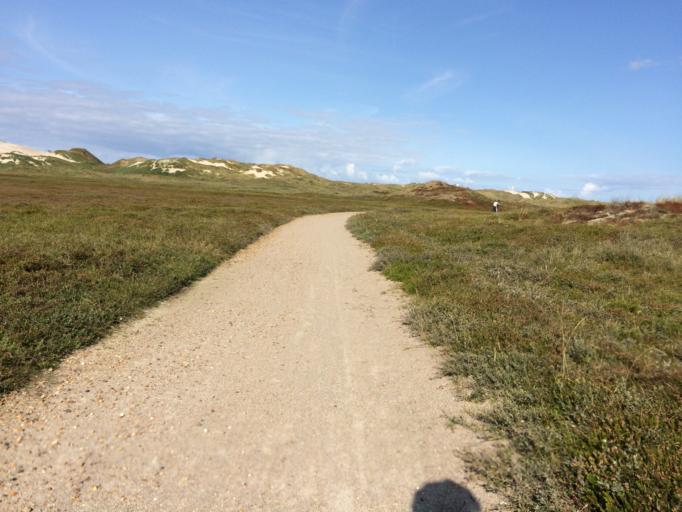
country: DK
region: Central Jutland
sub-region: Ringkobing-Skjern Kommune
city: Hvide Sande
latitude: 55.9184
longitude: 8.1581
